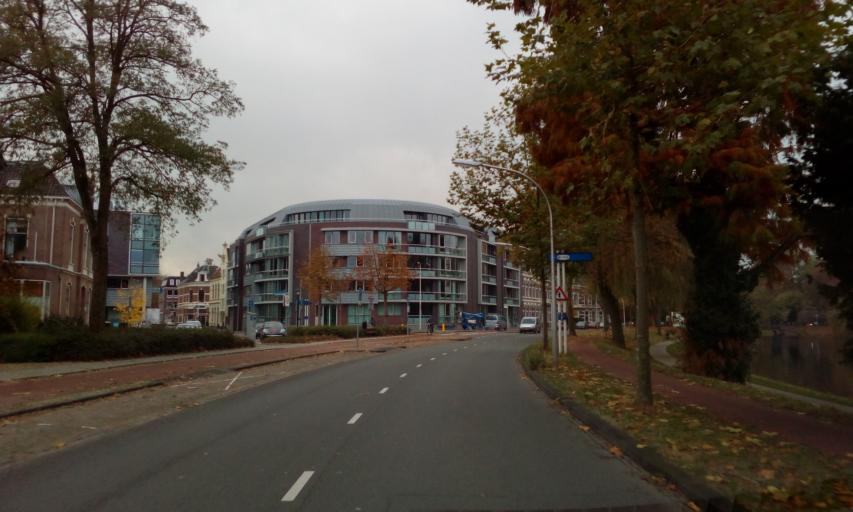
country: NL
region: Overijssel
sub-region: Gemeente Deventer
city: Deventer
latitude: 52.2571
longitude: 6.1536
